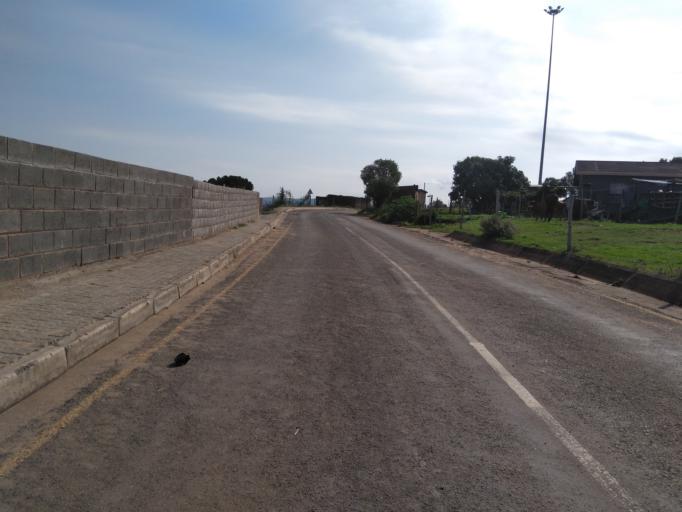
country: LS
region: Butha-Buthe
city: Butha-Buthe
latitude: -28.7732
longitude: 28.2497
